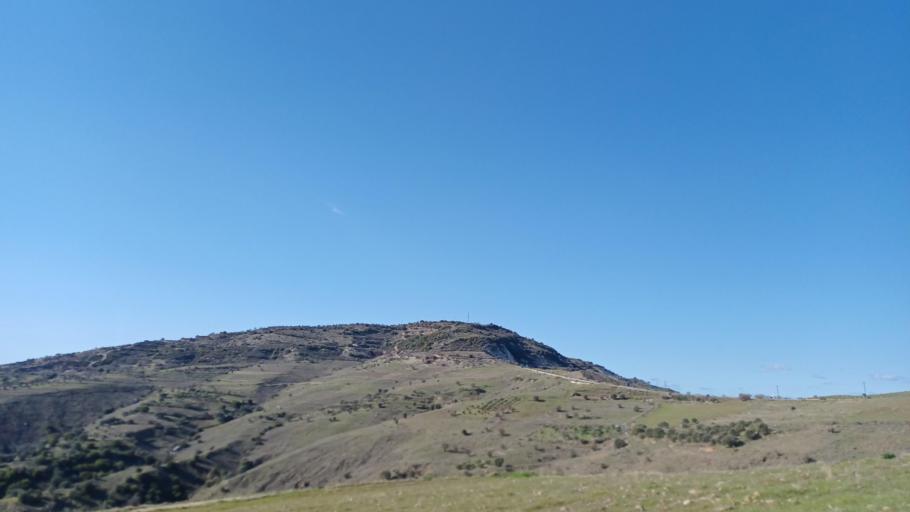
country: CY
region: Limassol
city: Pachna
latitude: 34.8229
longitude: 32.6879
